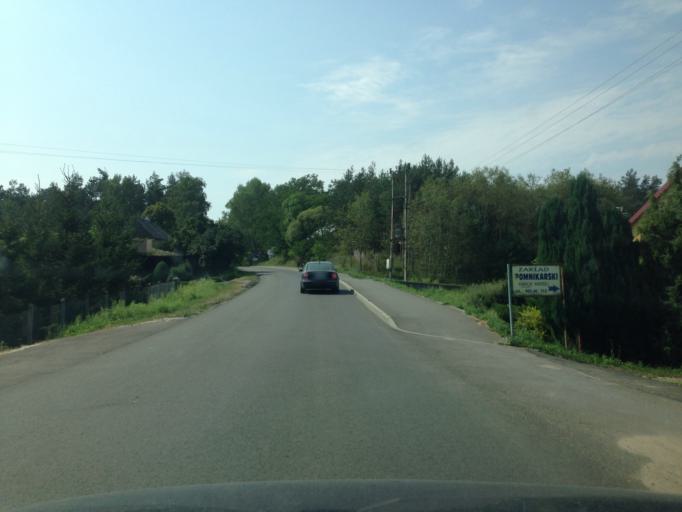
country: PL
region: Kujawsko-Pomorskie
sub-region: Powiat golubsko-dobrzynski
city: Golub-Dobrzyn
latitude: 53.0947
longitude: 19.0410
